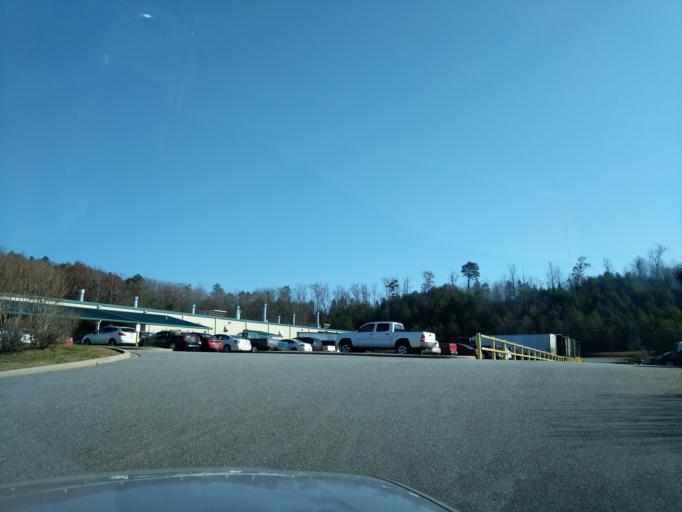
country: US
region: North Carolina
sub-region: McDowell County
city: West Marion
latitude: 35.6456
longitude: -81.9905
